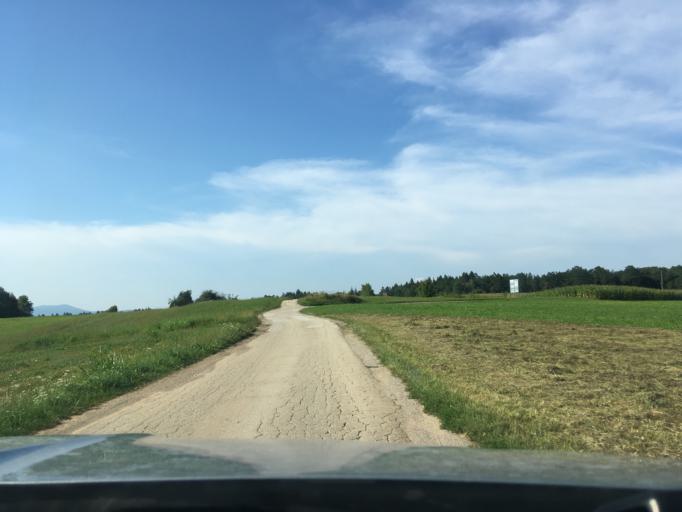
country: SI
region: Crnomelj
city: Crnomelj
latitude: 45.4762
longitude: 15.2083
